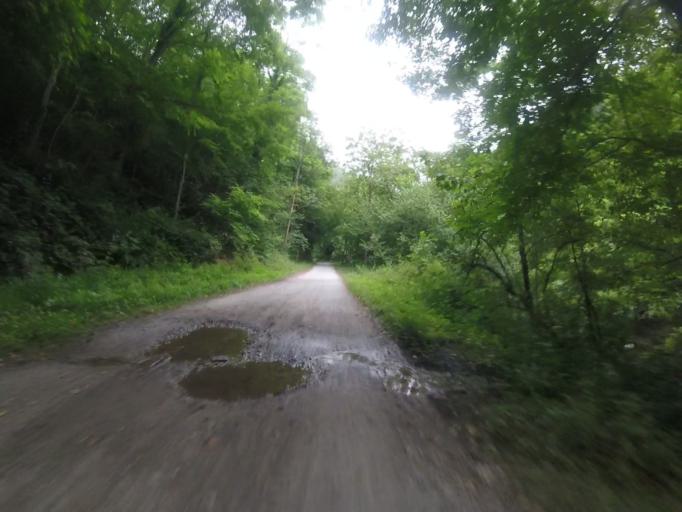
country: ES
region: Navarre
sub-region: Provincia de Navarra
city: Sunbilla
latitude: 43.2036
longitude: -1.6658
